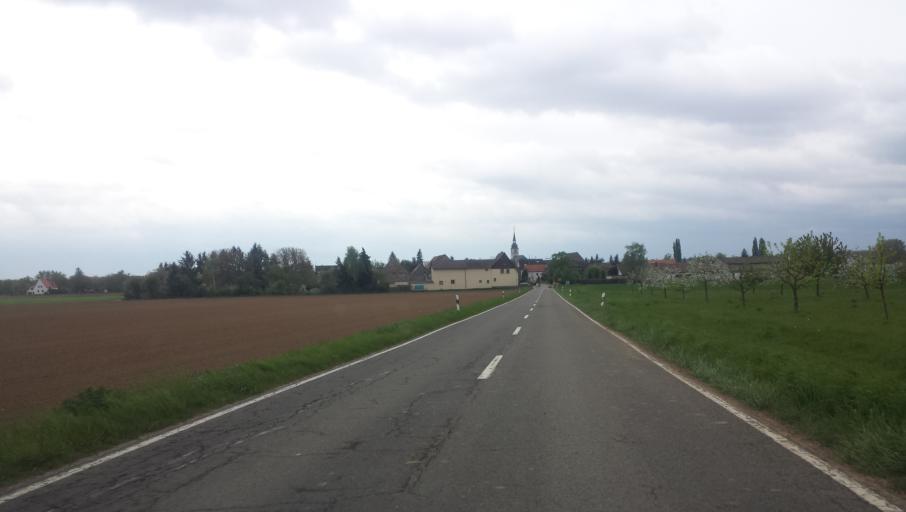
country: DE
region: Rheinland-Pfalz
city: Westheim
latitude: 49.2541
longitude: 8.3242
